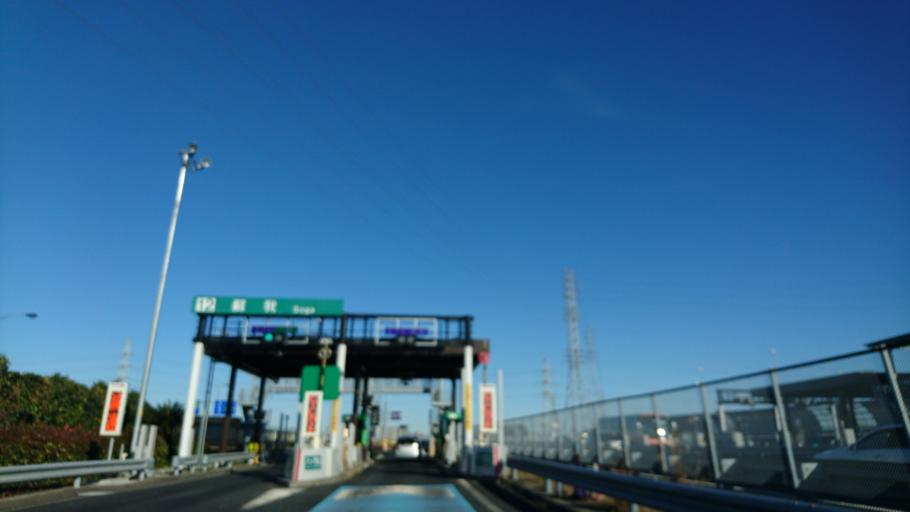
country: JP
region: Chiba
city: Chiba
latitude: 35.5612
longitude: 140.1385
